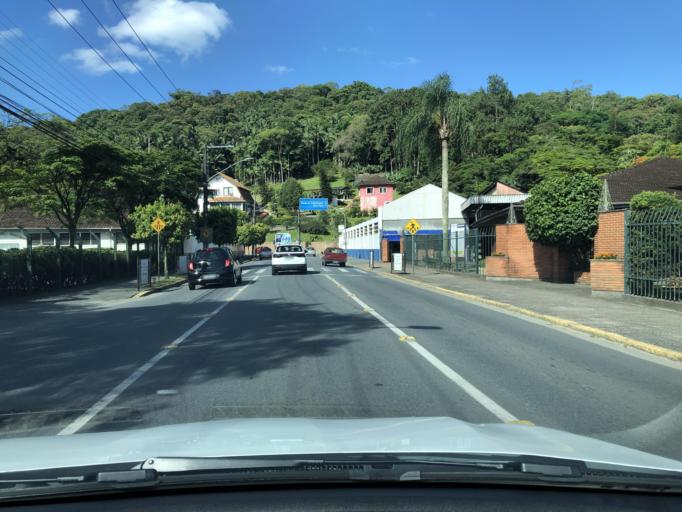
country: BR
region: Santa Catarina
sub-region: Joinville
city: Joinville
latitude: -26.3052
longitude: -48.8393
